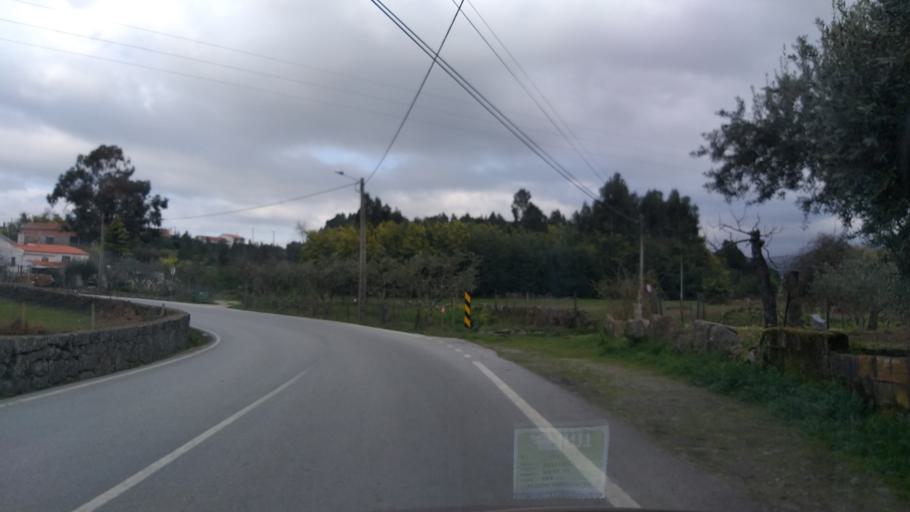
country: PT
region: Guarda
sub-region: Manteigas
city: Manteigas
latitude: 40.5013
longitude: -7.6146
